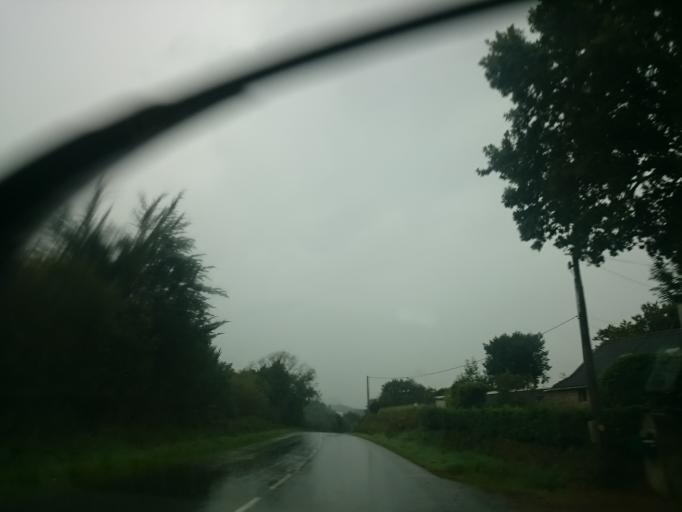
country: FR
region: Brittany
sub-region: Departement du Finistere
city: Plouvien
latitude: 48.5355
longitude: -4.4765
